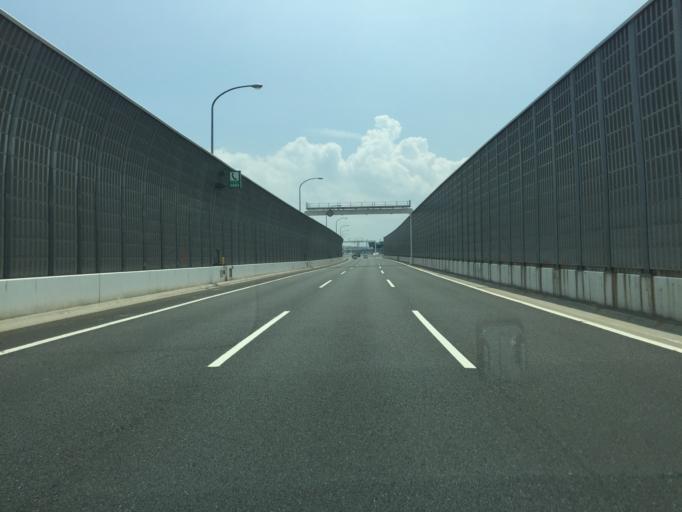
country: JP
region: Kanagawa
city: Yokohama
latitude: 35.4280
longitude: 139.6713
